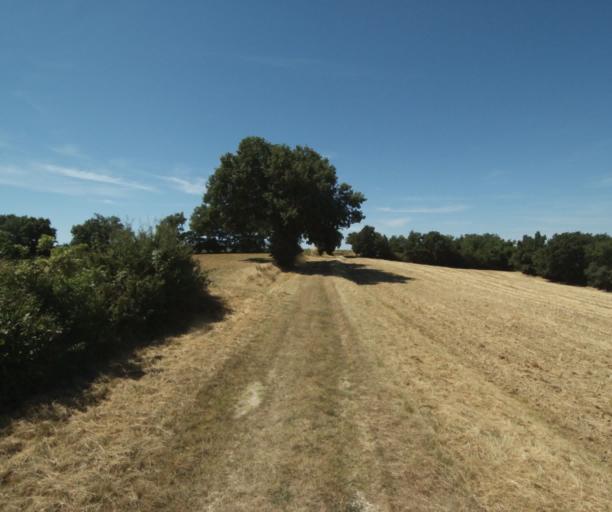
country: FR
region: Midi-Pyrenees
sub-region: Departement de la Haute-Garonne
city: Saint-Felix-Lauragais
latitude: 43.4840
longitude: 1.9208
